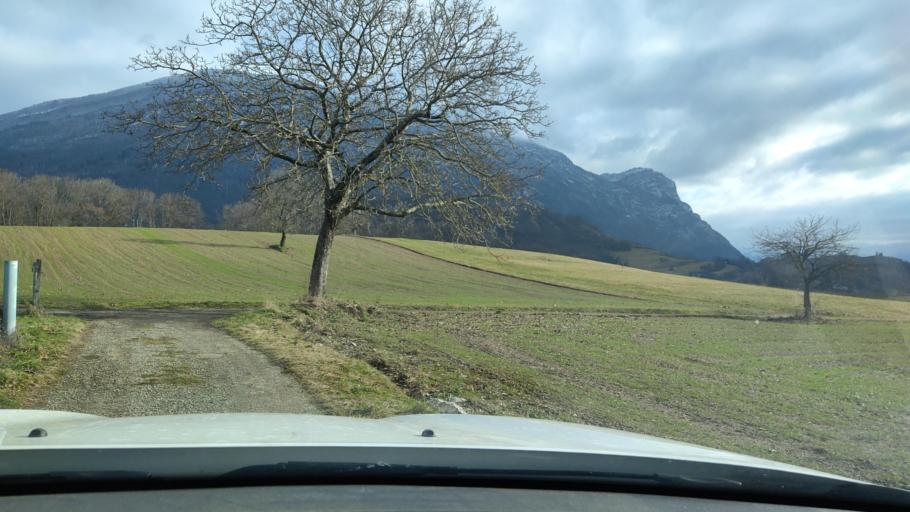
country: FR
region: Rhone-Alpes
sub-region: Departement de la Savoie
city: Challes-les-Eaux
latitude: 45.5379
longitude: 5.9854
